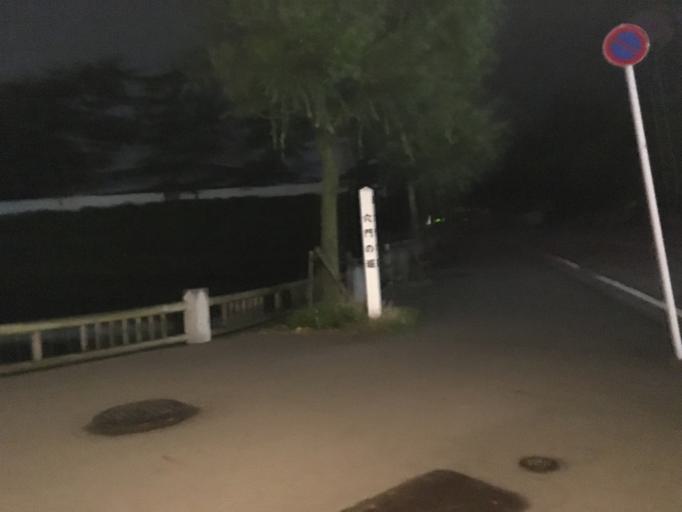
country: JP
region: Akita
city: Akita
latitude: 39.7181
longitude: 140.1219
